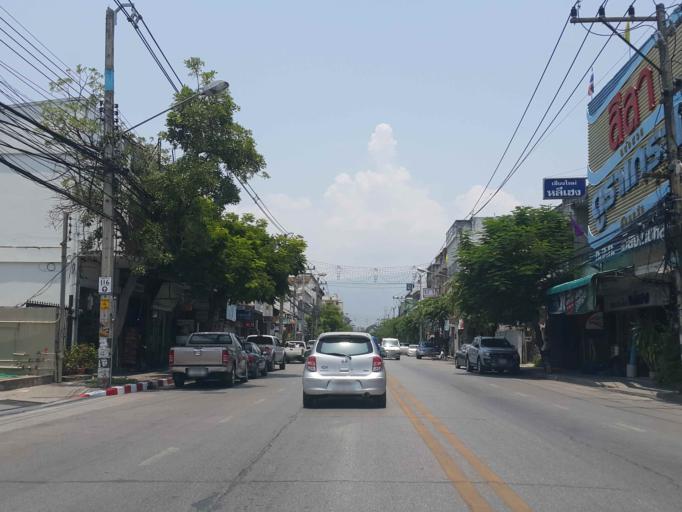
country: TH
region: Chiang Mai
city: Chiang Mai
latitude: 18.7864
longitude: 99.0117
